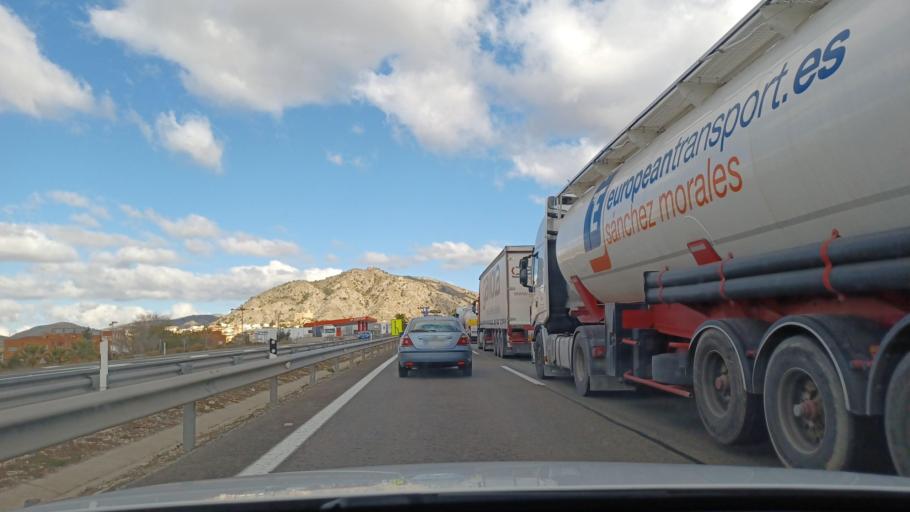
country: ES
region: Valencia
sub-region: Provincia de Alicante
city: Elda
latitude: 38.4724
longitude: -0.7720
